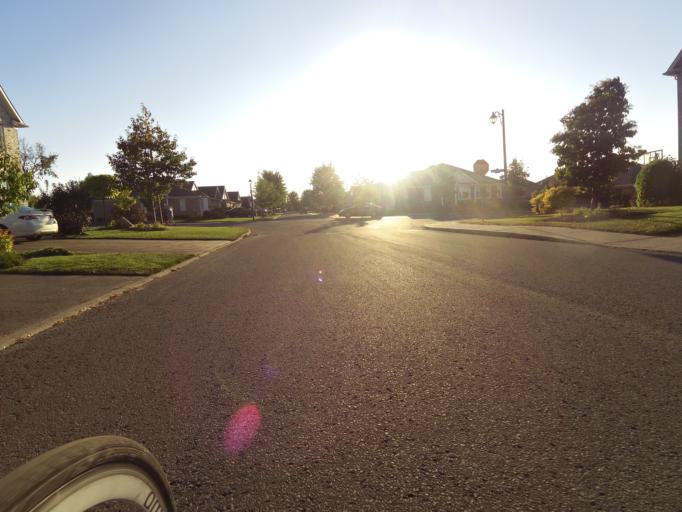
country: CA
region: Ontario
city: Bells Corners
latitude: 45.2499
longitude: -75.7266
